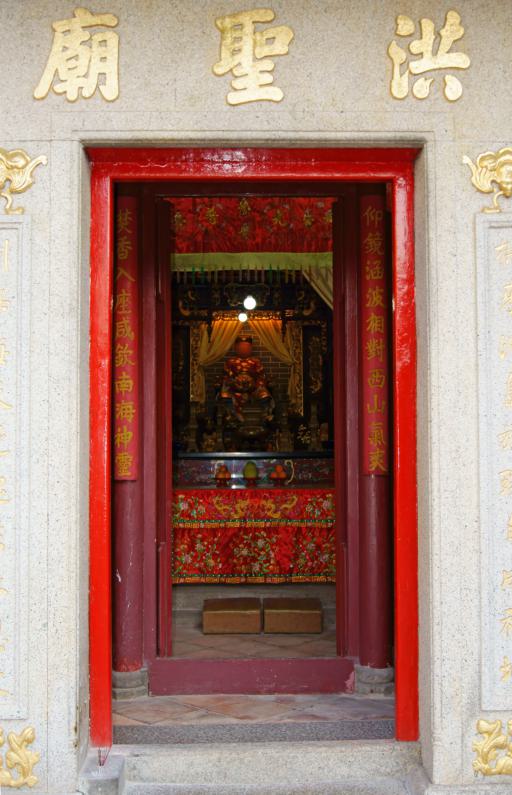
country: HK
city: Yung Shue Wan
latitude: 22.2047
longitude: 114.0272
